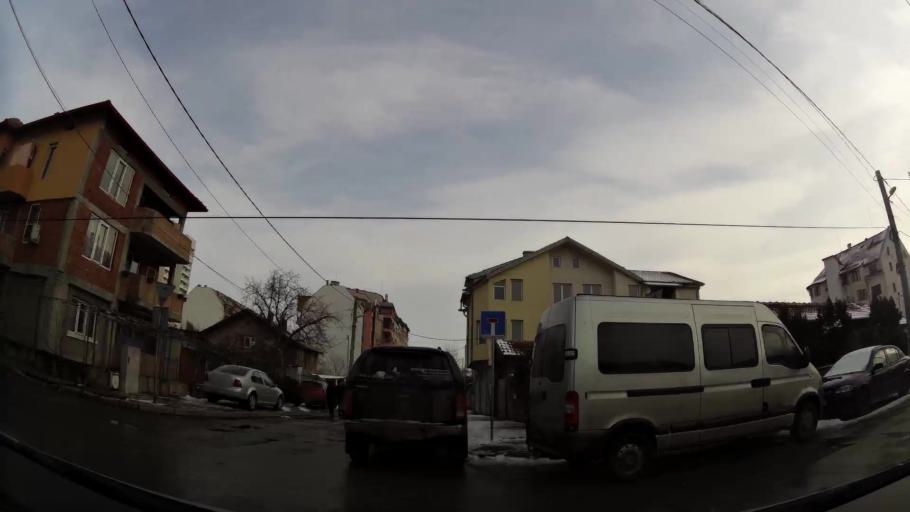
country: BG
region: Sofia-Capital
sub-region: Stolichna Obshtina
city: Sofia
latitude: 42.7073
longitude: 23.3611
